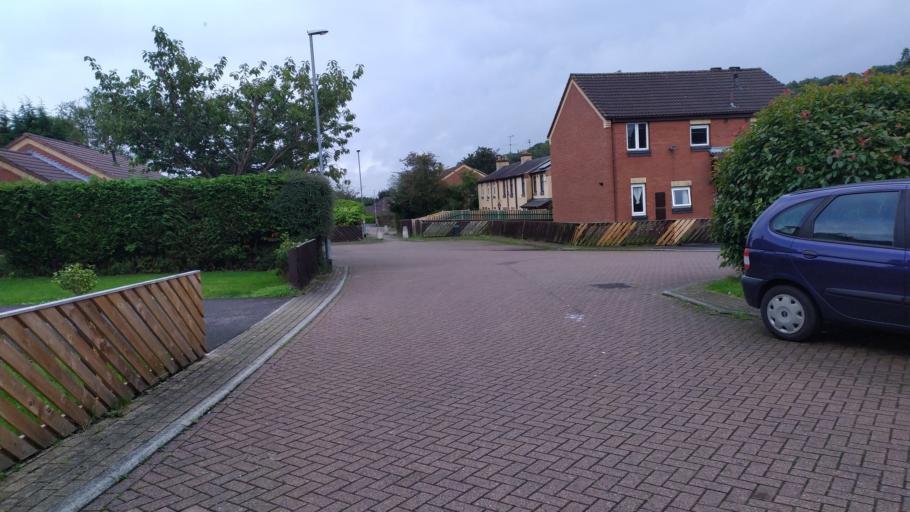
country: GB
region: England
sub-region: City and Borough of Leeds
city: Chapel Allerton
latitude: 53.8229
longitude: -1.5602
